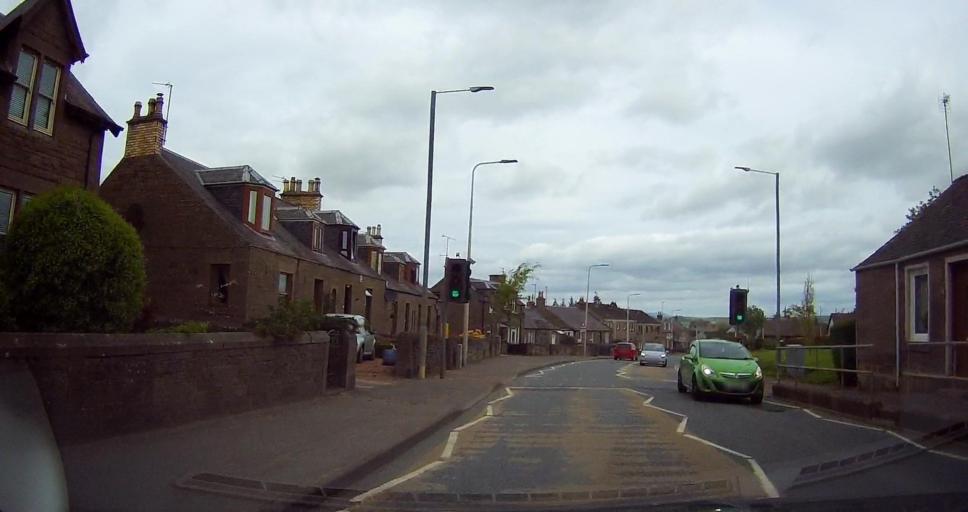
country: GB
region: Scotland
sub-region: Angus
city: Forfar
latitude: 56.6376
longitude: -2.8944
